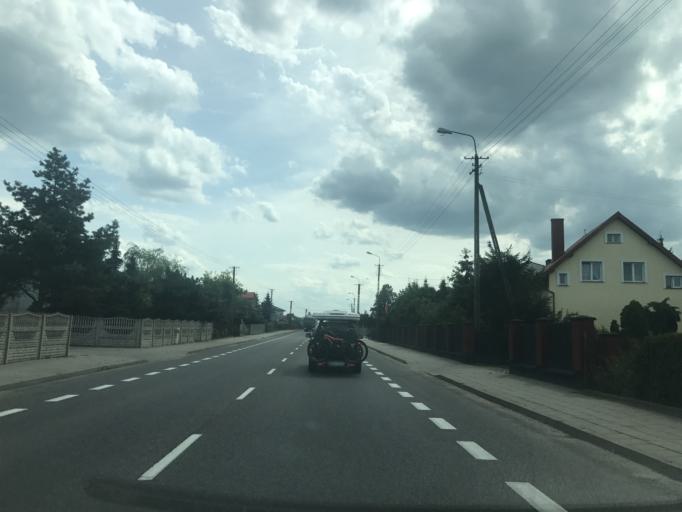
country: PL
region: Masovian Voivodeship
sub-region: Powiat mlawski
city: Wisniewo
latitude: 53.0629
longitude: 20.3475
